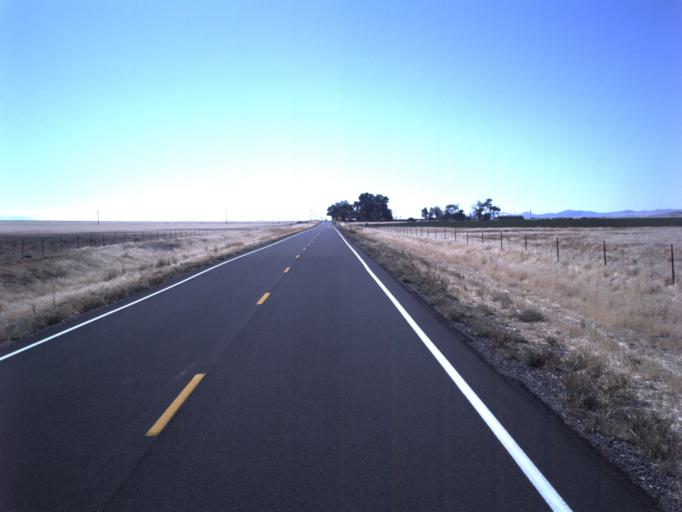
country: US
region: Utah
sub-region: Tooele County
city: Grantsville
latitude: 40.4408
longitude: -112.7487
